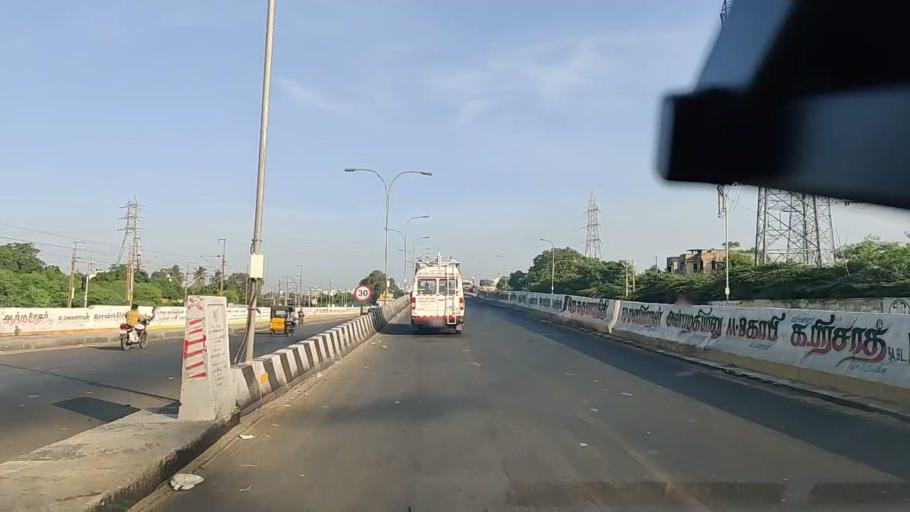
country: IN
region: Tamil Nadu
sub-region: Chennai
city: George Town
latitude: 13.1072
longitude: 80.2691
